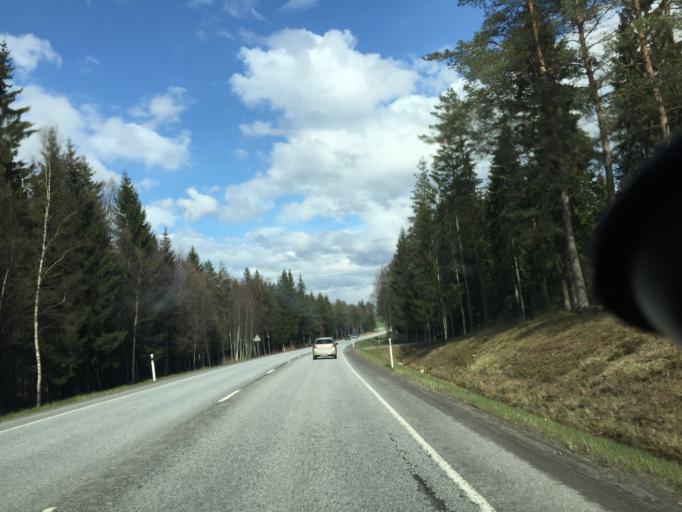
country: FI
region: Uusimaa
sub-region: Raaseporin
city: Karis
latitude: 60.0354
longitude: 23.5996
